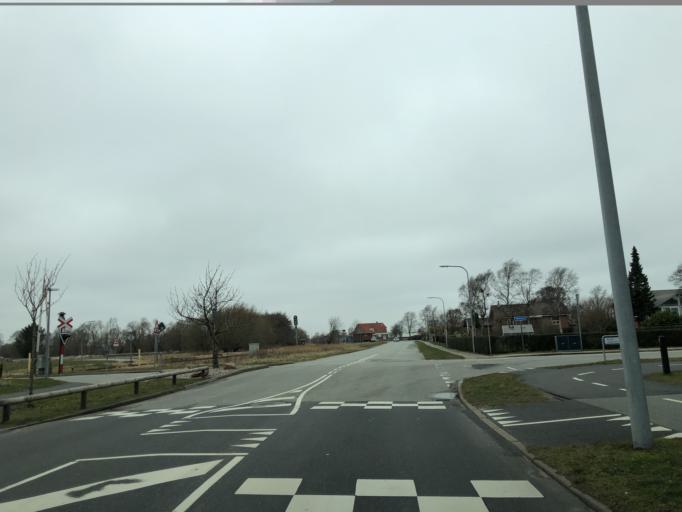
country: DK
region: North Denmark
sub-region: Frederikshavn Kommune
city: Strandby
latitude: 57.4882
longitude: 10.4930
